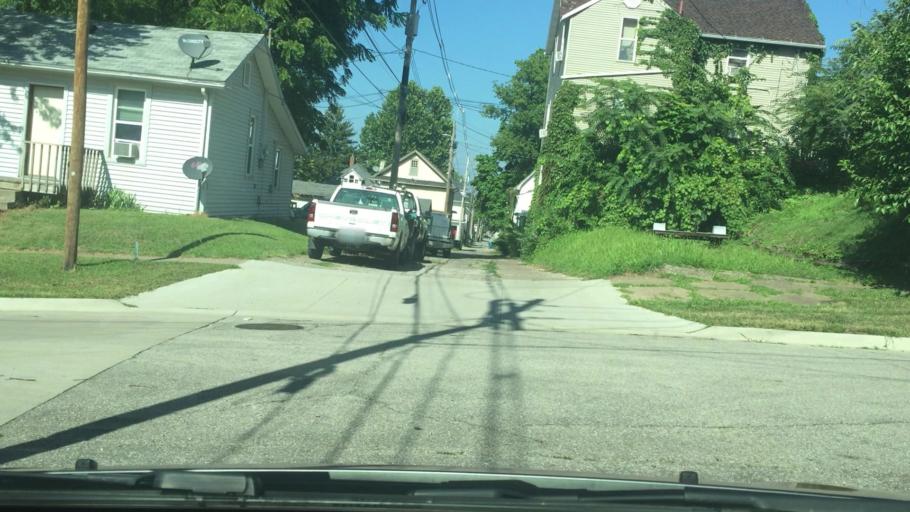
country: US
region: Iowa
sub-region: Muscatine County
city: Muscatine
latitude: 41.4208
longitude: -91.0520
